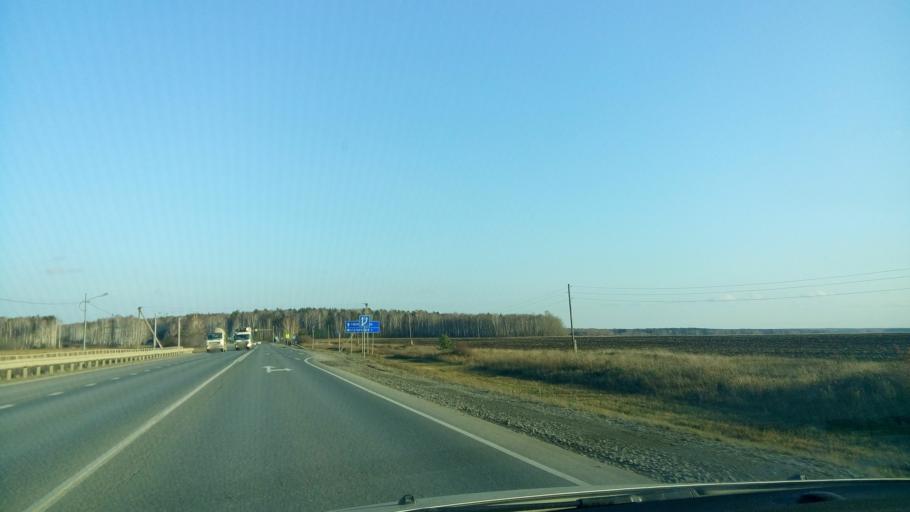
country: RU
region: Sverdlovsk
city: Verkhneye Dubrovo
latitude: 56.7410
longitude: 61.1807
